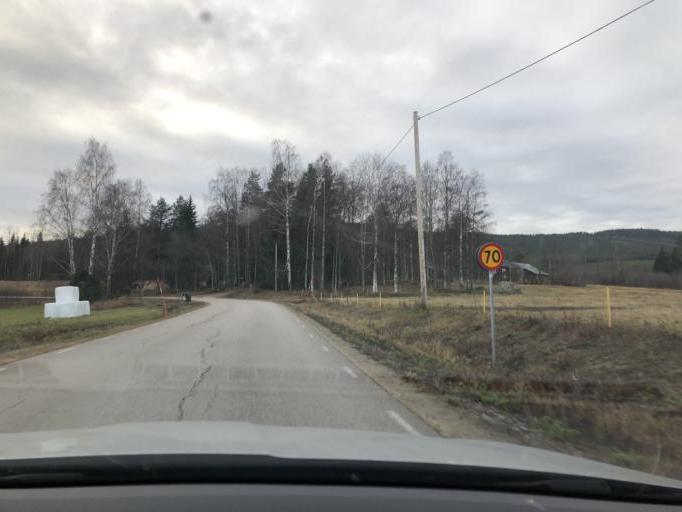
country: SE
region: Gaevleborg
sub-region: Hudiksvalls Kommun
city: Sorforsa
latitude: 61.6738
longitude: 16.9226
